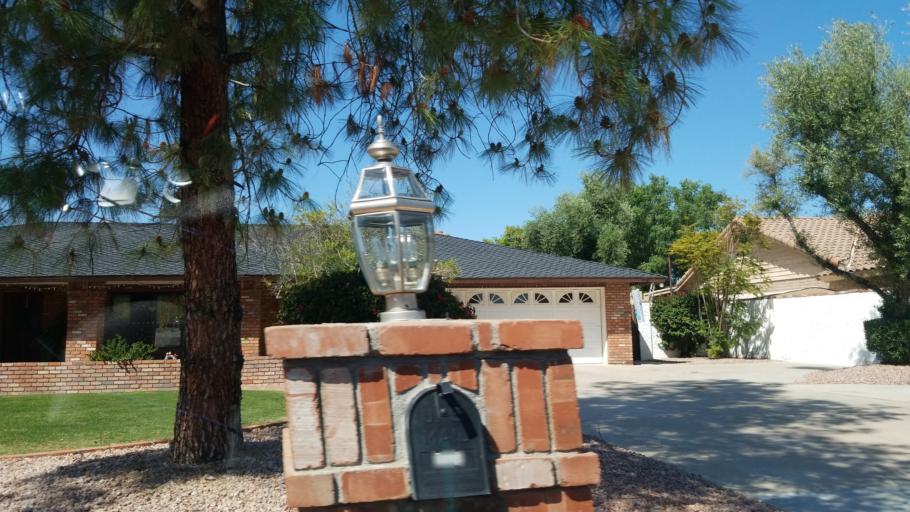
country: US
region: Arizona
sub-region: Maricopa County
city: Paradise Valley
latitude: 33.5920
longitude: -112.0278
